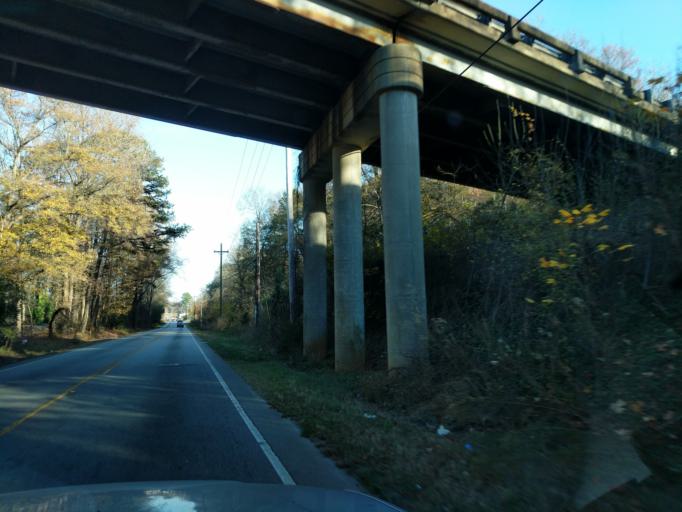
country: US
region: South Carolina
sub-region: Spartanburg County
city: Fairforest
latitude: 34.9563
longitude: -82.0045
